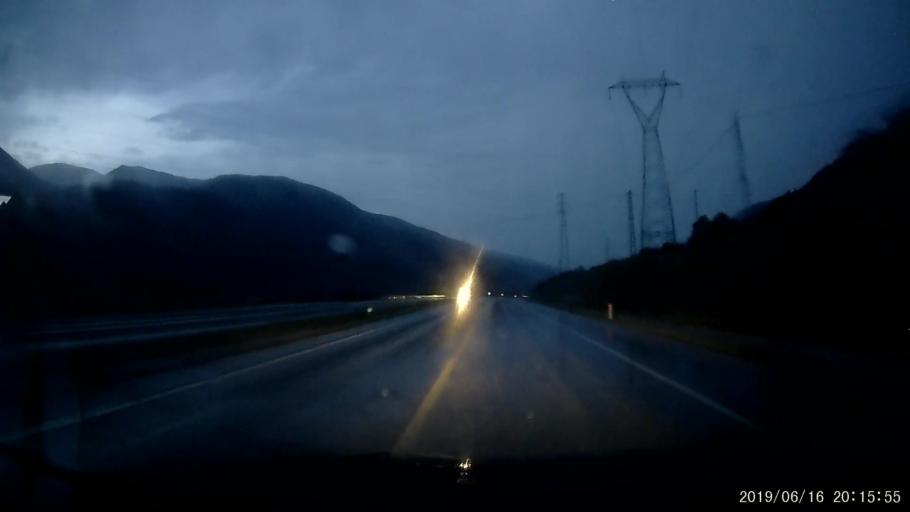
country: TR
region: Tokat
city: Resadiye
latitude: 40.3562
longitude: 37.4534
